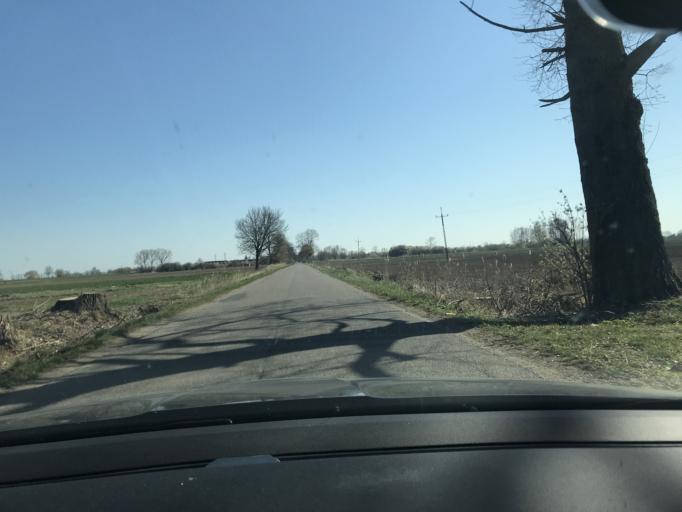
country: PL
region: Pomeranian Voivodeship
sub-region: Powiat nowodworski
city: Sztutowo
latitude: 54.3226
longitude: 19.1580
